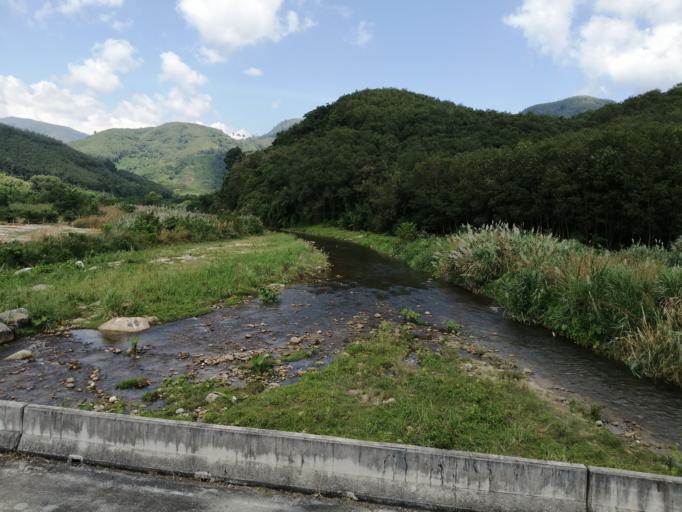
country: TH
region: Nakhon Si Thammarat
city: Phipun
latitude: 8.5974
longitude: 99.5207
